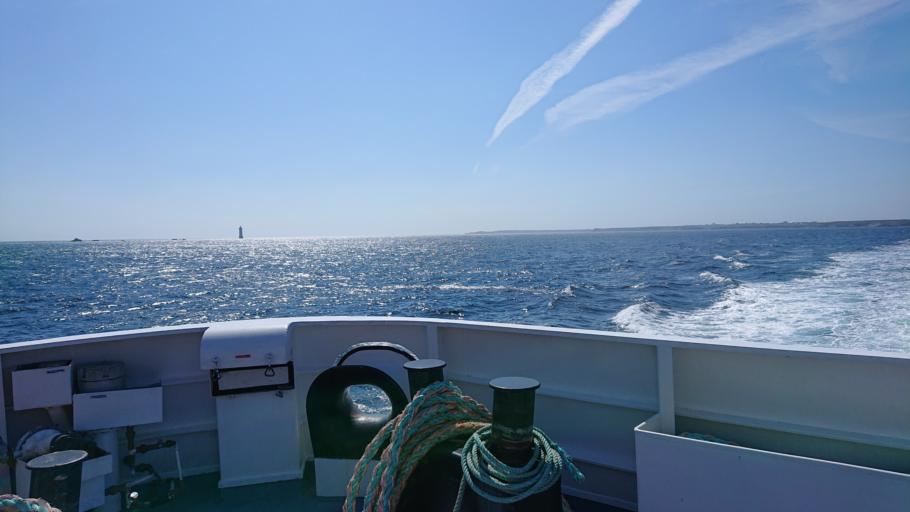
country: FR
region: Brittany
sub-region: Departement du Finistere
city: Porspoder
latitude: 48.4469
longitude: -4.9997
